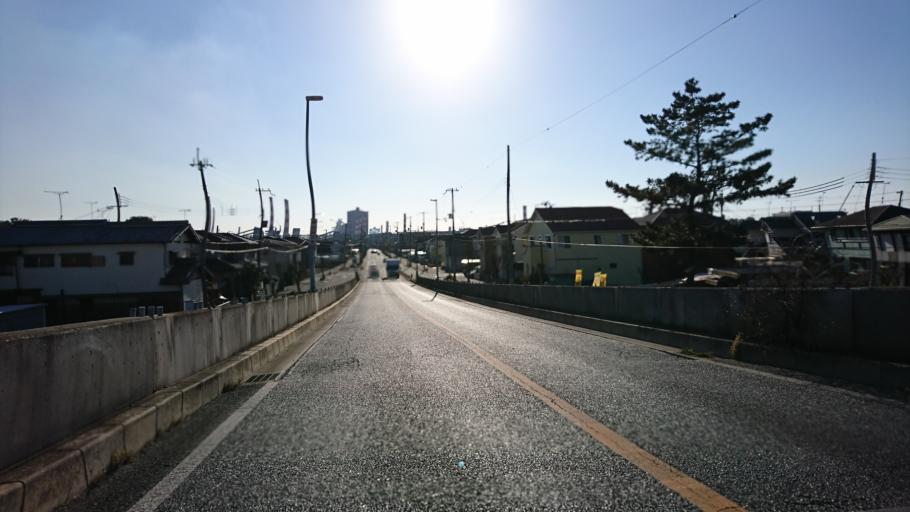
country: JP
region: Hyogo
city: Kakogawacho-honmachi
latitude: 34.7344
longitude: 134.8395
